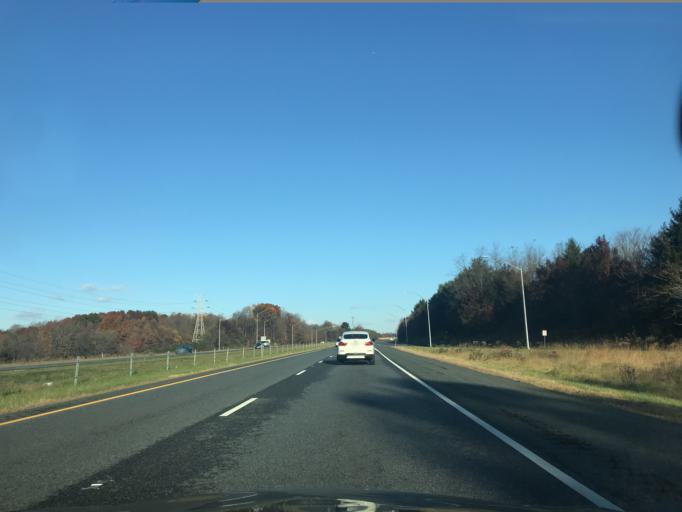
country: US
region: Maryland
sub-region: Baltimore County
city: Reisterstown
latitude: 39.4434
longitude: -76.8249
